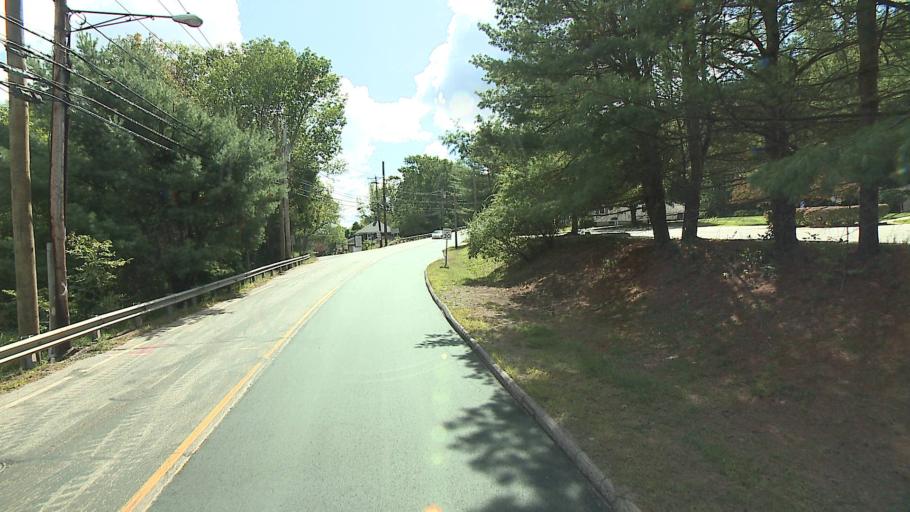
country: US
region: Connecticut
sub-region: Windham County
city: Putnam
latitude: 41.9103
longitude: -71.9152
